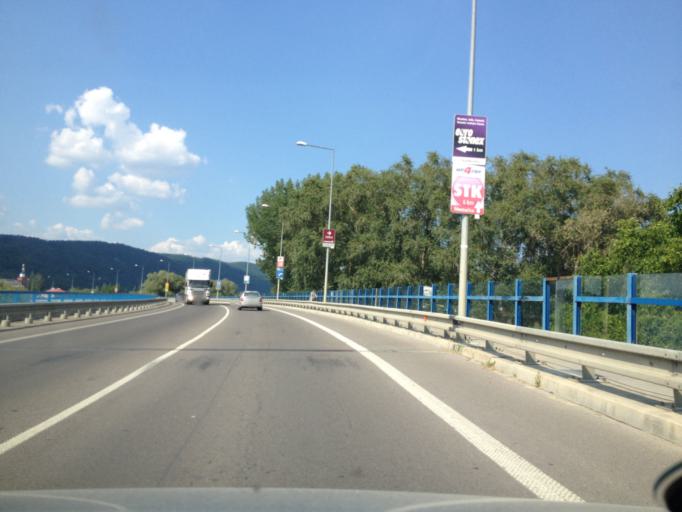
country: SK
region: Nitriansky
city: Puchov
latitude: 49.1120
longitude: 18.3163
